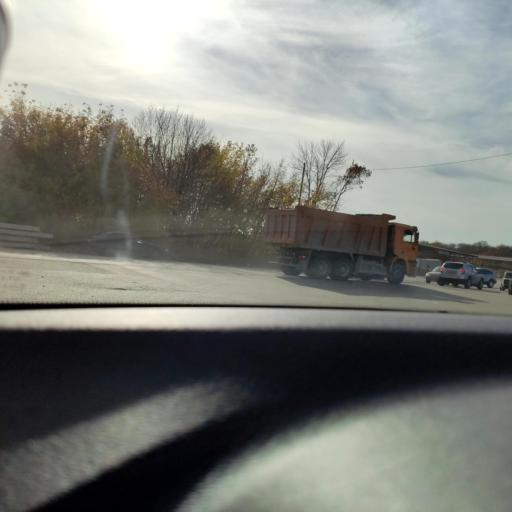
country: RU
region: Samara
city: Petra-Dubrava
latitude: 53.2722
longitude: 50.2741
